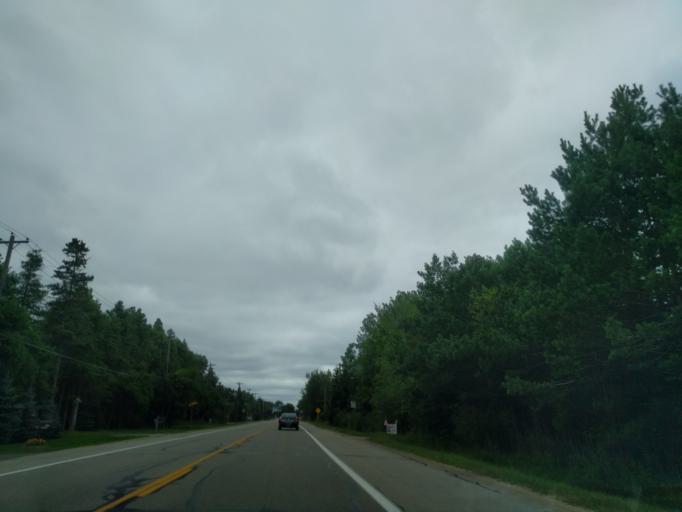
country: US
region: Michigan
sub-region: Delta County
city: Escanaba
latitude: 45.6928
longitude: -87.1005
